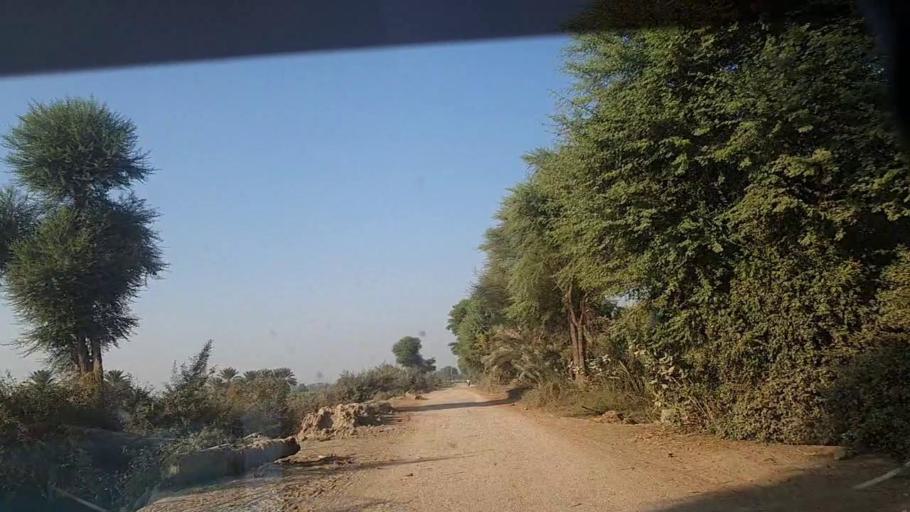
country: PK
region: Sindh
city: Sobhadero
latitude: 27.2603
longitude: 68.3507
